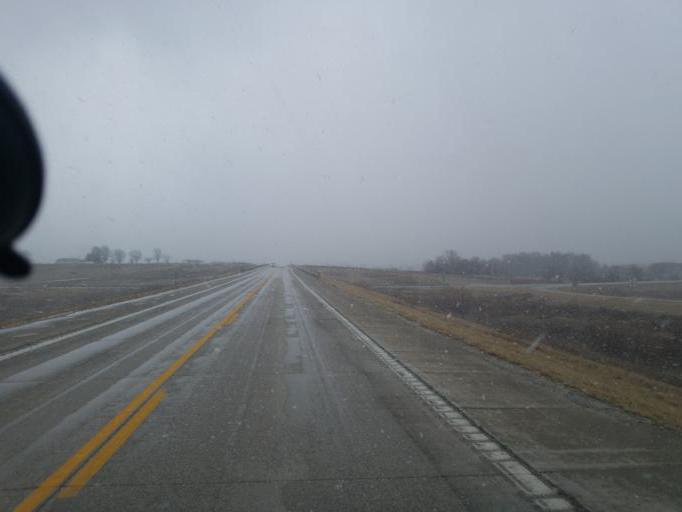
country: US
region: Missouri
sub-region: Adair County
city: Kirksville
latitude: 40.2396
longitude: -92.5792
